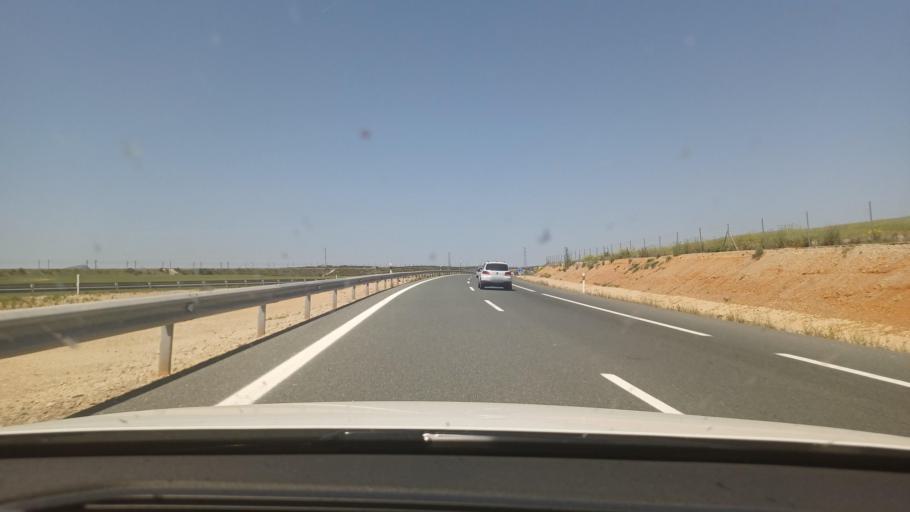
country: ES
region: Castille-La Mancha
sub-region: Provincia de Albacete
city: Alpera
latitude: 38.8781
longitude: -1.2347
